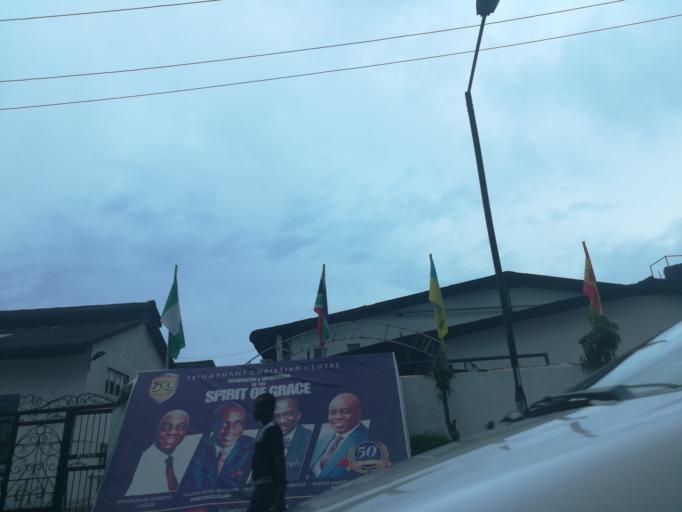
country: NG
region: Lagos
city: Agege
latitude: 6.6138
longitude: 3.3334
